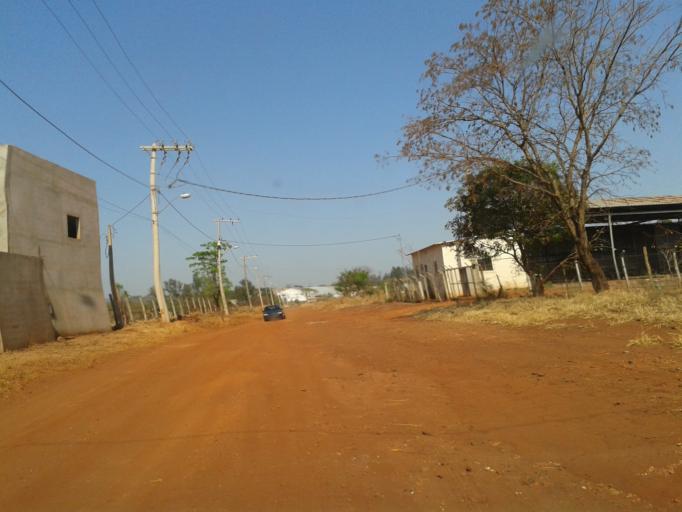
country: BR
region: Minas Gerais
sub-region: Ituiutaba
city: Ituiutaba
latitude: -18.9604
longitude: -49.4868
